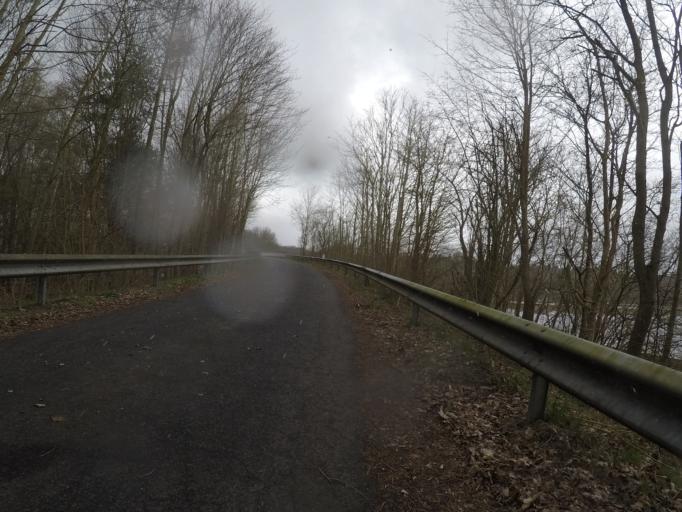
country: DE
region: Lower Saxony
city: Langen
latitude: 53.6247
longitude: 8.6667
